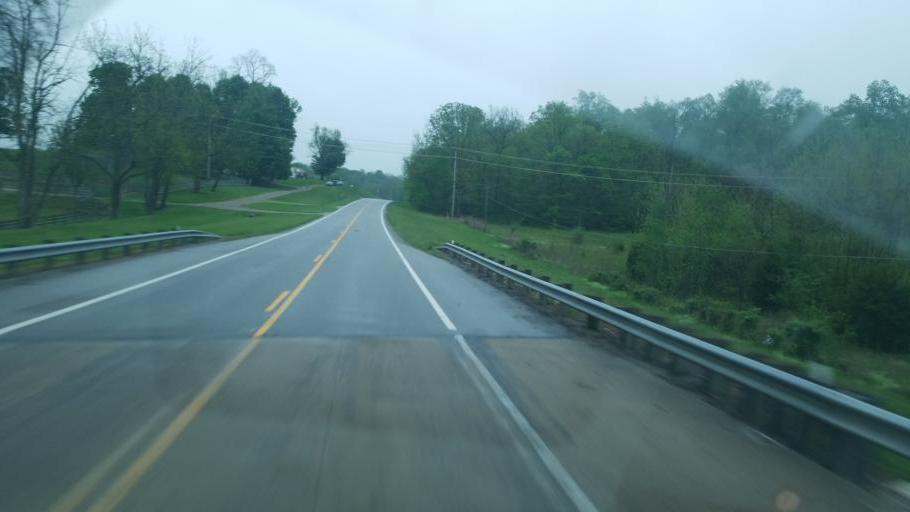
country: US
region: Ohio
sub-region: Highland County
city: Hillsboro
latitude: 39.1928
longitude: -83.6399
